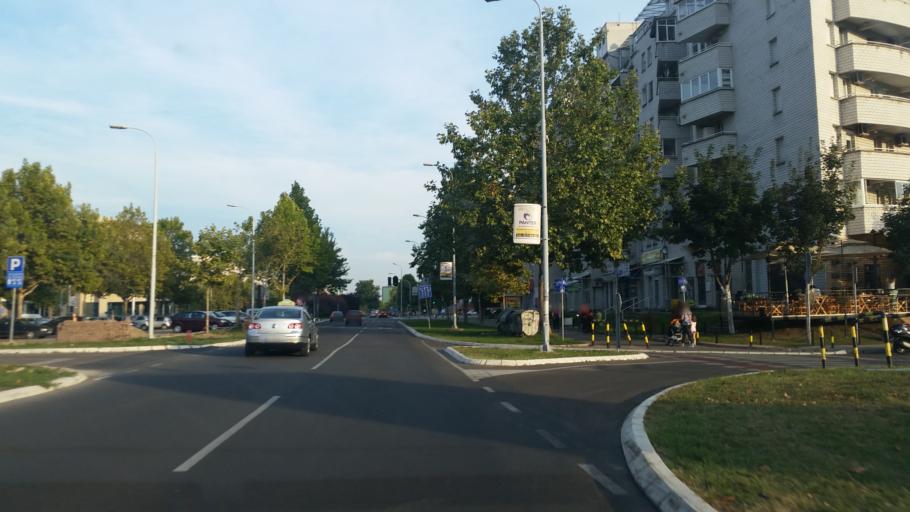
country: RS
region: Central Serbia
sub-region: Belgrade
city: Novi Beograd
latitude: 44.8149
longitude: 20.4237
